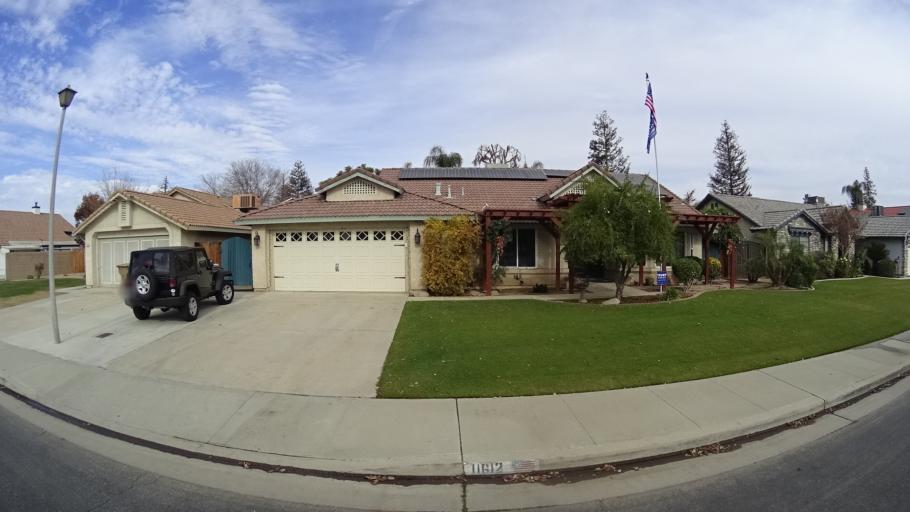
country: US
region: California
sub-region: Kern County
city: Rosedale
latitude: 35.3961
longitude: -119.1317
